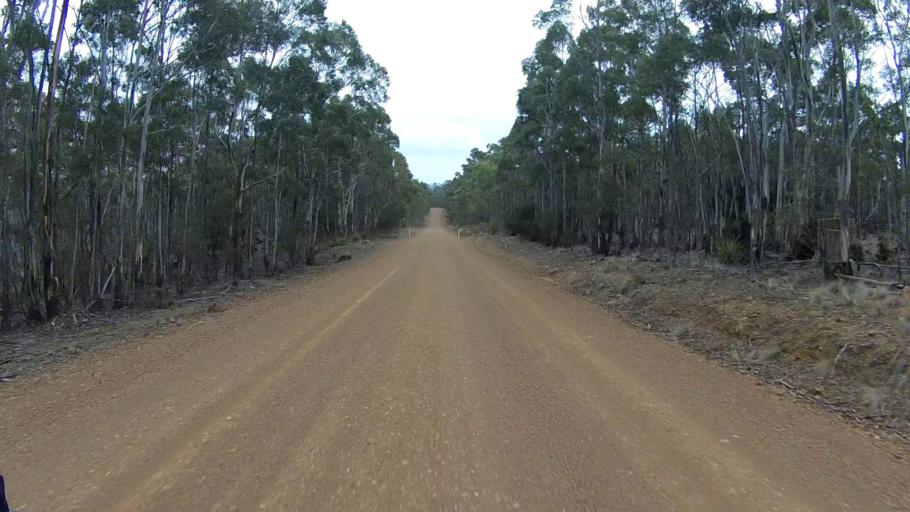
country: AU
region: Tasmania
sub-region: Sorell
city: Sorell
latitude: -42.5894
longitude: 147.8858
